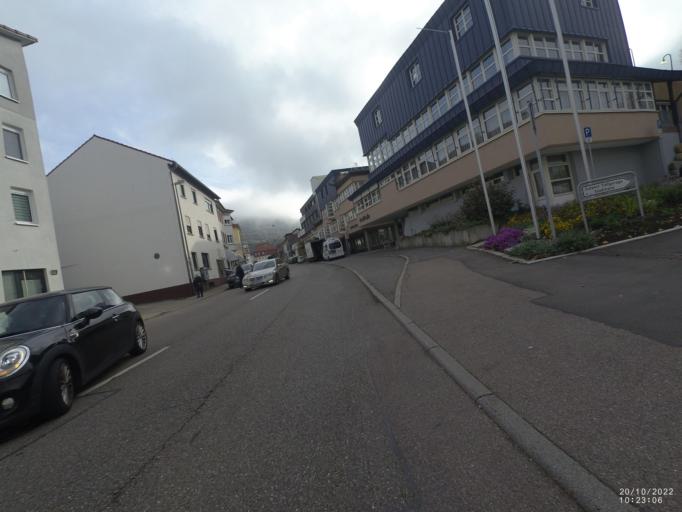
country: DE
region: Baden-Wuerttemberg
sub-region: Regierungsbezirk Stuttgart
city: Donzdorf
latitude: 48.6867
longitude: 9.8075
